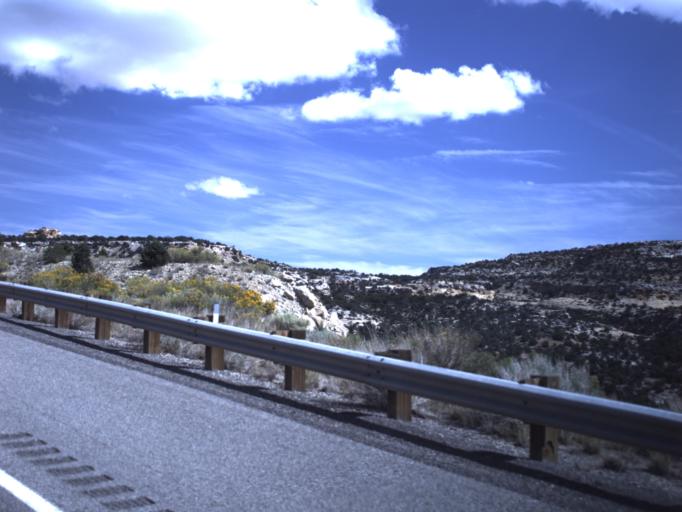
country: US
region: Utah
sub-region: Emery County
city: Ferron
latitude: 38.8595
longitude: -110.8192
